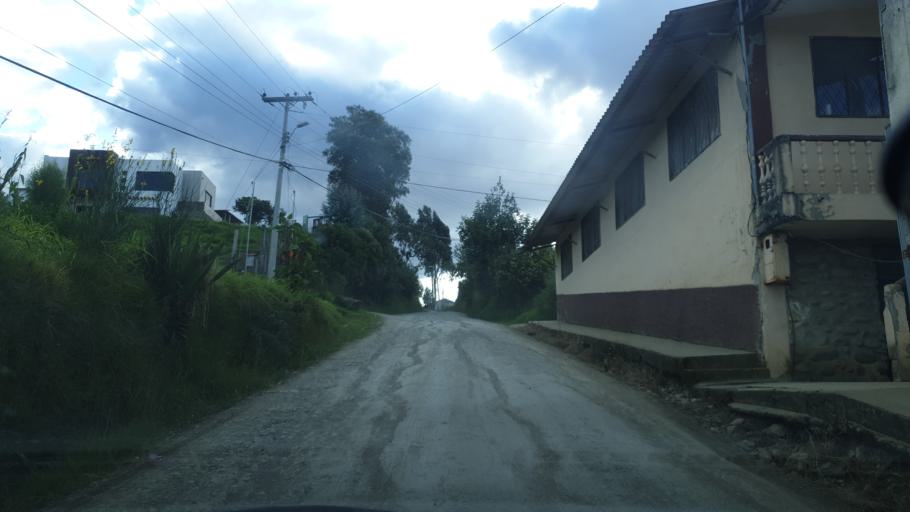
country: EC
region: Azuay
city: Cuenca
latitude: -2.9248
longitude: -78.9676
